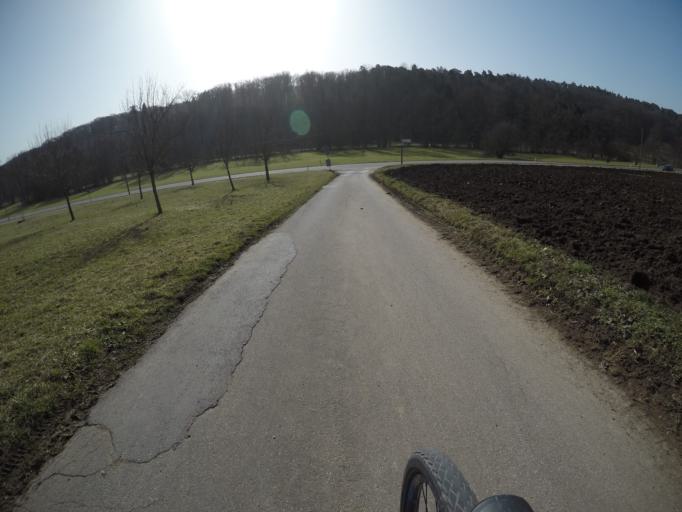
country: DE
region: Baden-Wuerttemberg
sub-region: Regierungsbezirk Stuttgart
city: Schonaich
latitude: 48.6519
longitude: 9.0837
